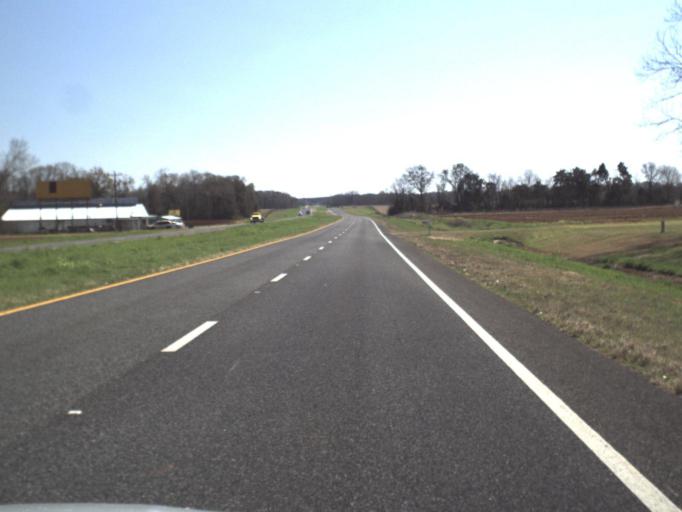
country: US
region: Florida
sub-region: Jackson County
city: Marianna
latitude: 30.8689
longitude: -85.3593
